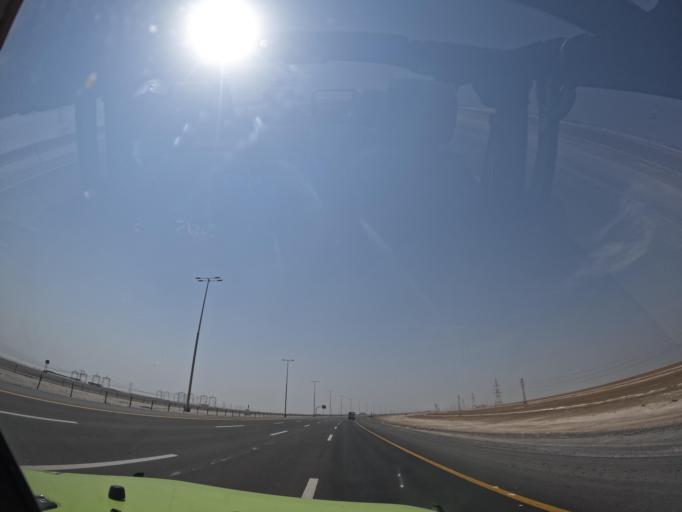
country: AE
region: Abu Dhabi
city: Abu Dhabi
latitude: 24.1583
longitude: 54.3461
